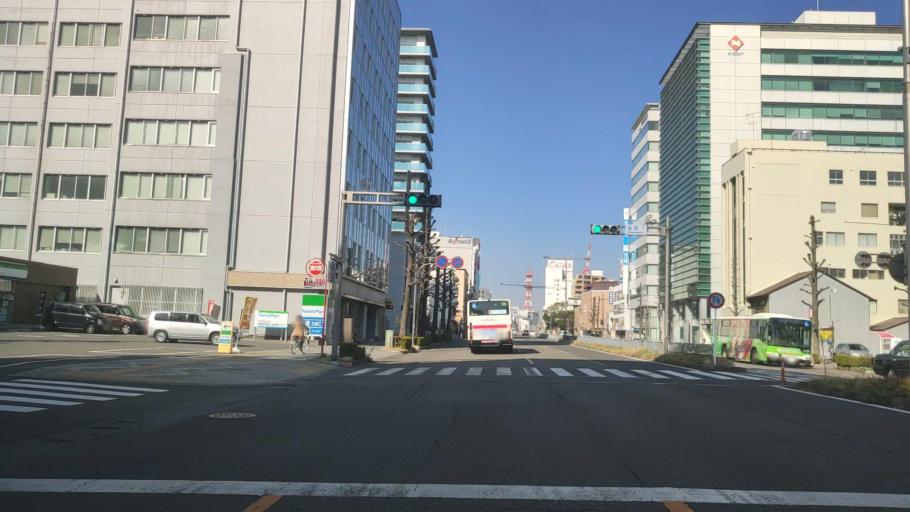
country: JP
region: Gifu
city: Gifu-shi
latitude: 35.4133
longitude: 136.7568
